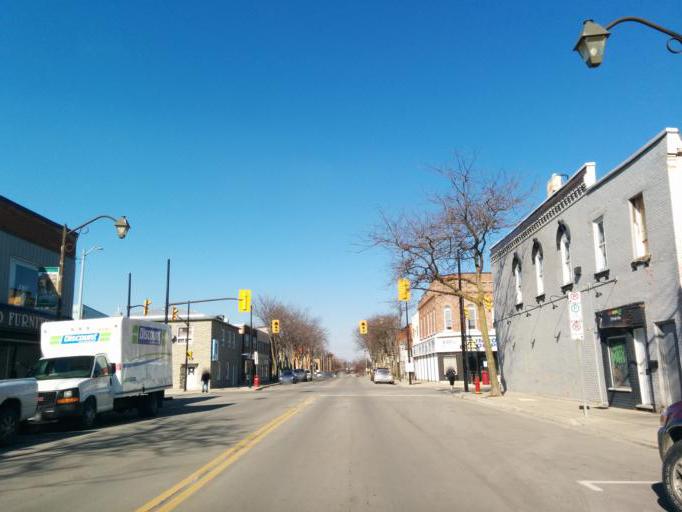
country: CA
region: Ontario
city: Norfolk County
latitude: 42.8364
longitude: -80.3061
